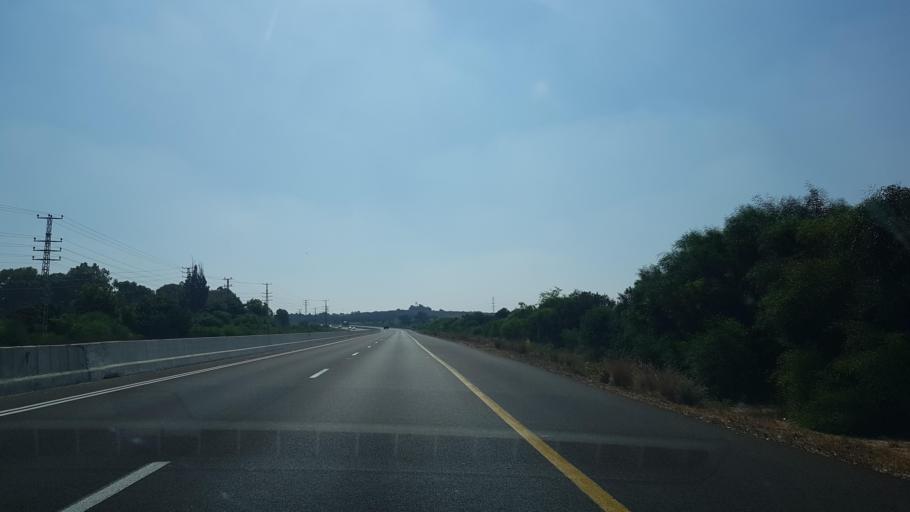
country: IL
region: Southern District
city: Ashqelon
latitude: 31.6888
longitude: 34.6695
